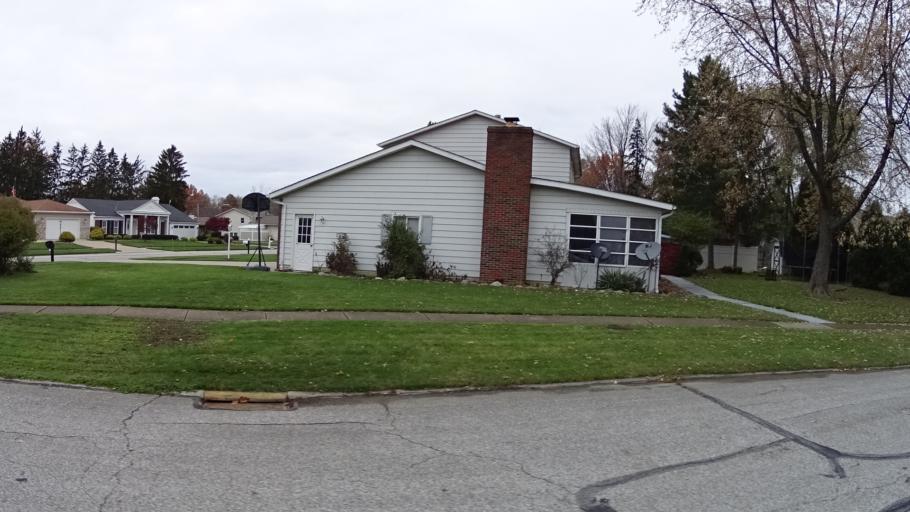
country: US
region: Ohio
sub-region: Lorain County
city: Sheffield
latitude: 41.4086
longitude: -82.0786
